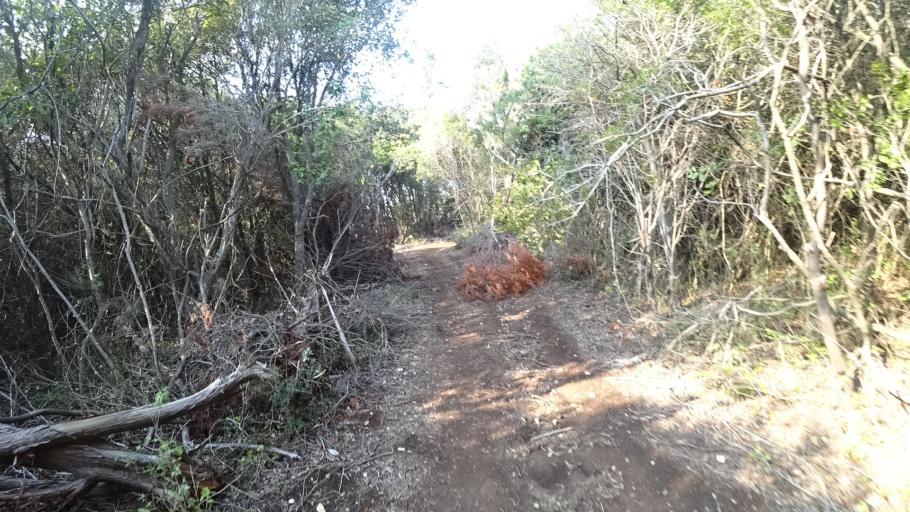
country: HR
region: Primorsko-Goranska
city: Mali Losinj
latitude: 44.4892
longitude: 14.5058
